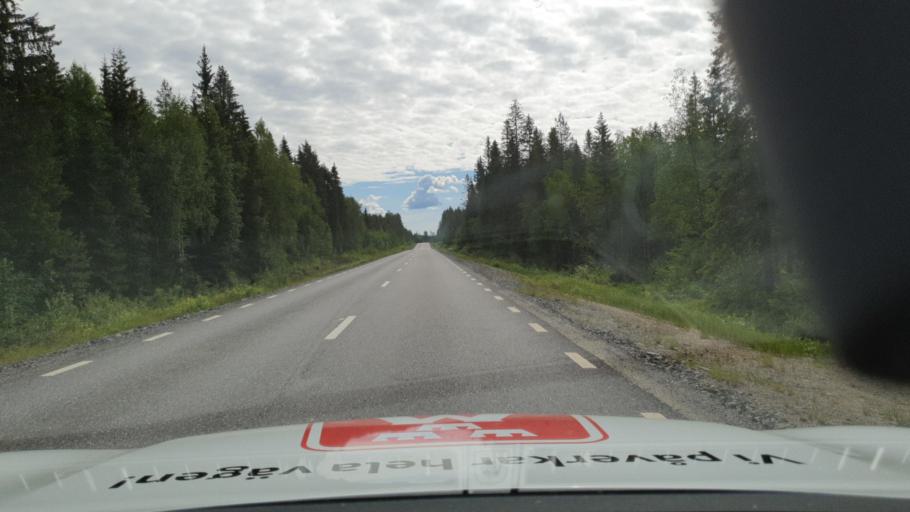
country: SE
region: Vaesterbotten
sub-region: Vindelns Kommun
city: Vindeln
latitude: 64.2534
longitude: 20.1293
